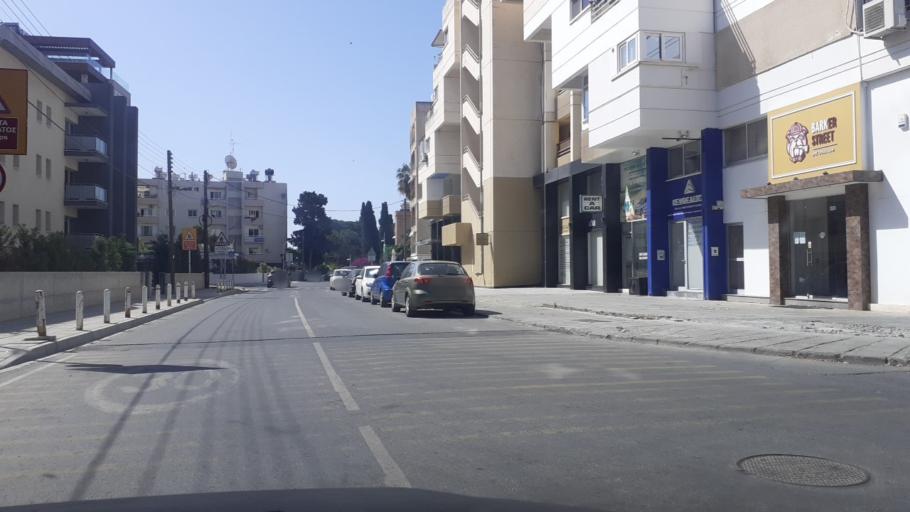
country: CY
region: Limassol
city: Mouttagiaka
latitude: 34.6963
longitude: 33.0859
